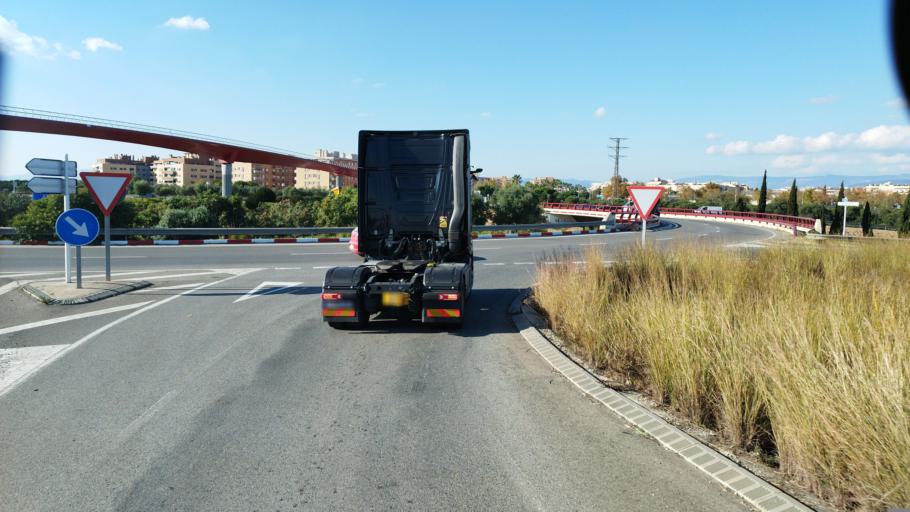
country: ES
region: Catalonia
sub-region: Provincia de Tarragona
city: Vila-seca
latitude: 41.1050
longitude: 1.1562
